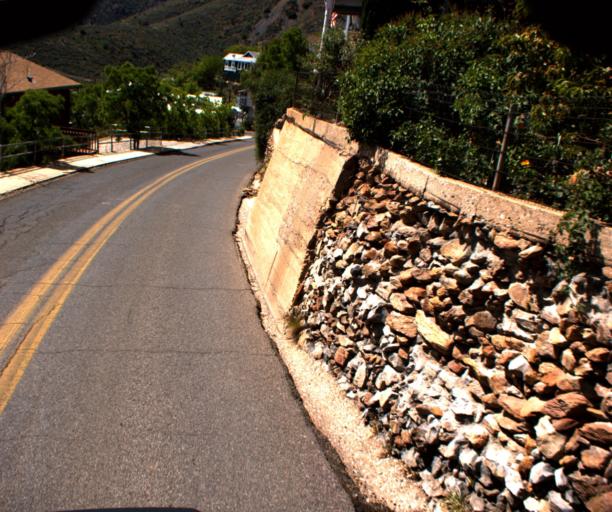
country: US
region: Arizona
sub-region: Yavapai County
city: Clarkdale
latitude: 34.7486
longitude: -112.1123
